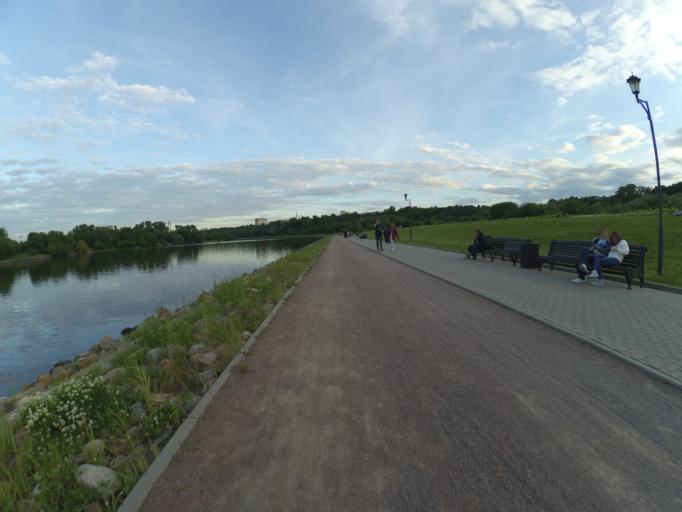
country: RU
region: Moscow
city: Kolomenskoye
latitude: 55.6598
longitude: 37.6706
